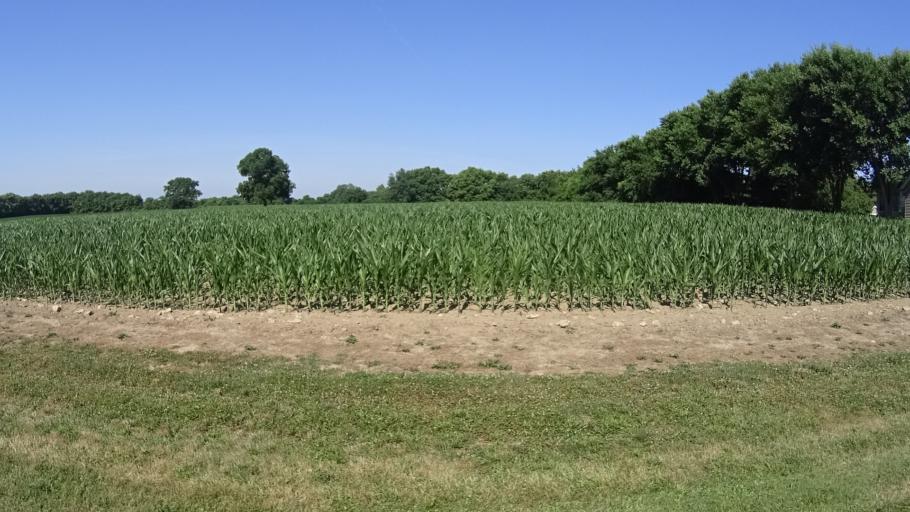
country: US
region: Ohio
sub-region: Huron County
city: Bellevue
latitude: 41.3683
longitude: -82.7949
